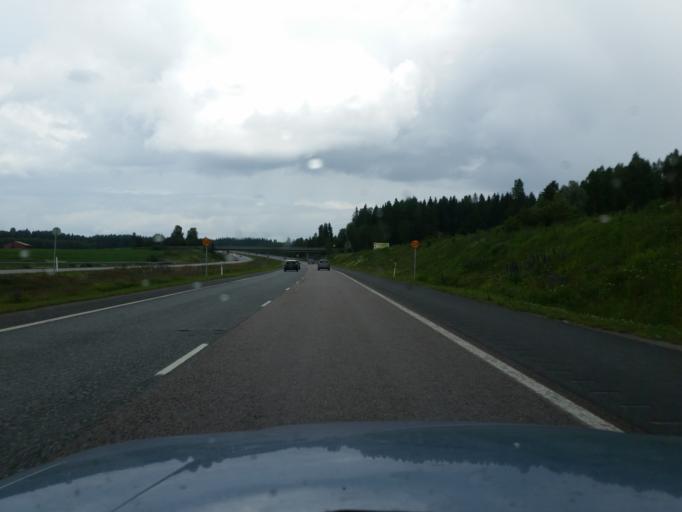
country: FI
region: Paijanne Tavastia
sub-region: Lahti
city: Nastola
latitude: 61.0733
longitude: 25.8851
